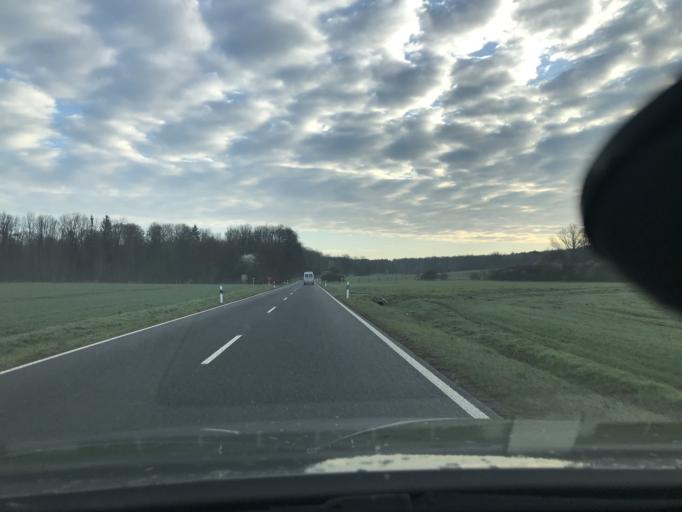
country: DE
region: Thuringia
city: Menteroda
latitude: 51.2802
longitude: 10.5365
